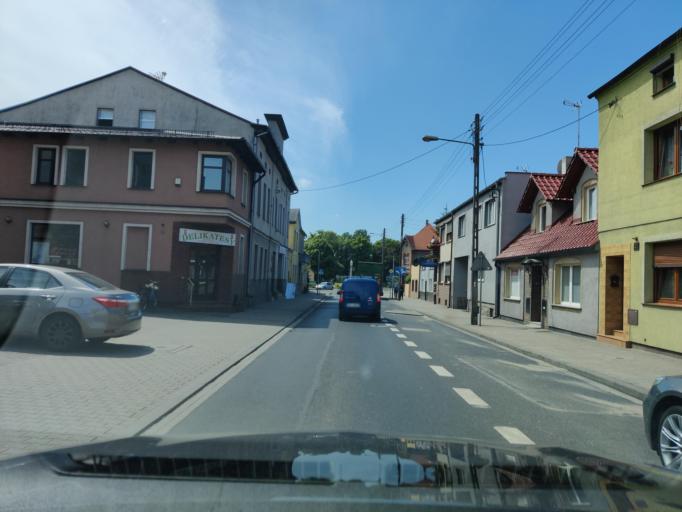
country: PL
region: Greater Poland Voivodeship
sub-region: Powiat grodziski
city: Rakoniewice
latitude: 52.1374
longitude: 16.2722
